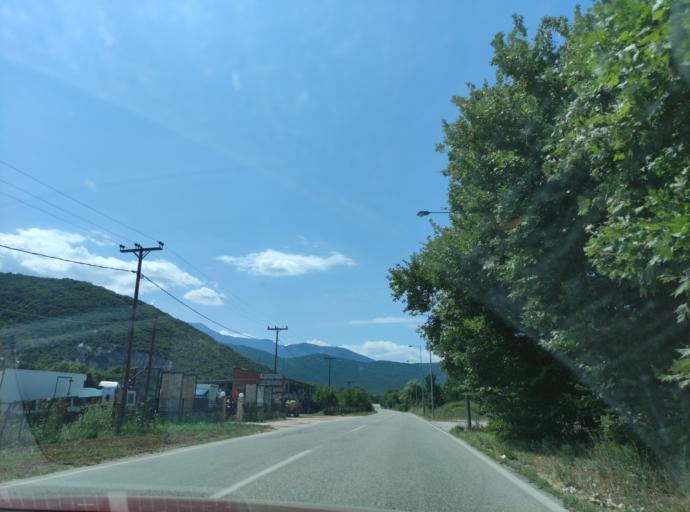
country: GR
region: East Macedonia and Thrace
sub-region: Nomos Kavalas
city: Palaiochori
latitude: 40.9518
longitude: 24.2020
